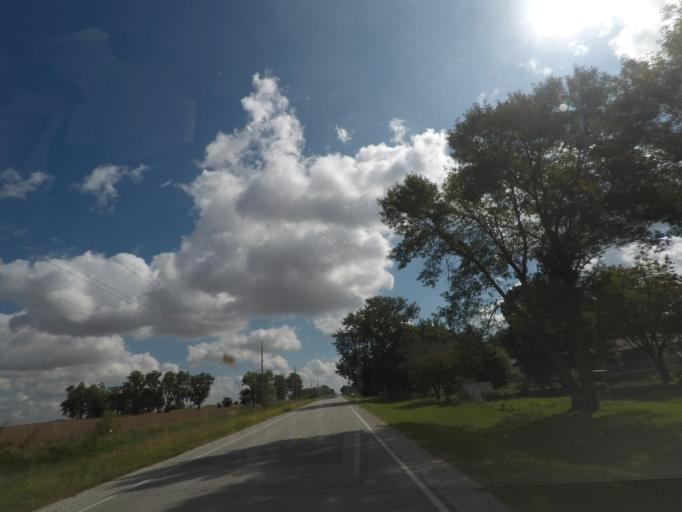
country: US
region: Iowa
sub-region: Story County
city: Nevada
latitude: 42.0225
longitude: -93.3215
